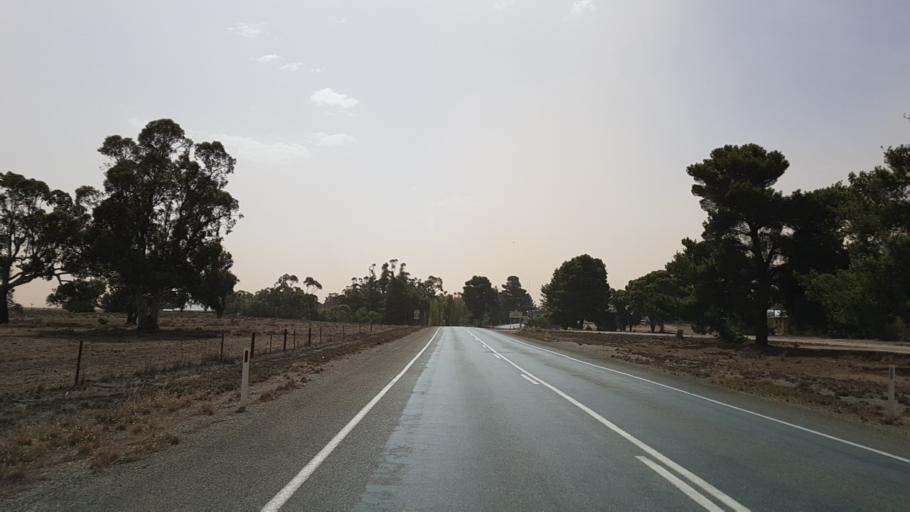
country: AU
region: South Australia
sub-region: Northern Areas
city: Jamestown
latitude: -33.4161
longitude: 138.8927
